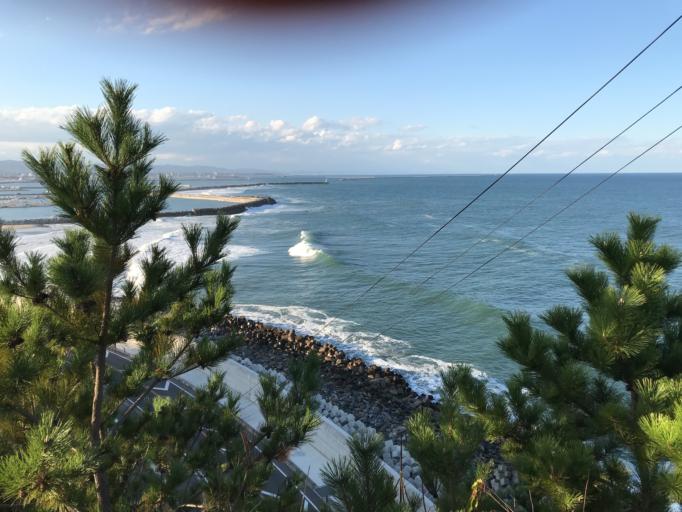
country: JP
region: Miyagi
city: Marumori
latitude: 37.8235
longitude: 140.9849
